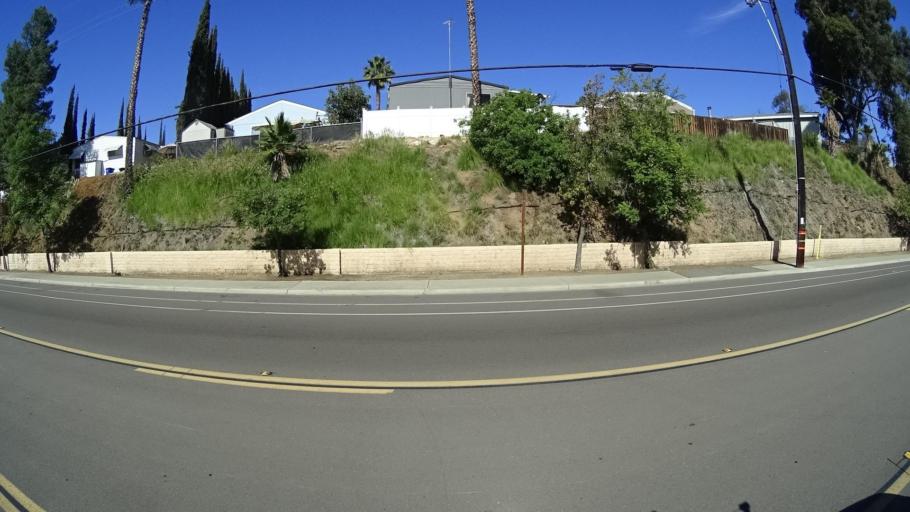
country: US
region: California
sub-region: San Diego County
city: Lakeside
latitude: 32.8345
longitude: -116.9033
